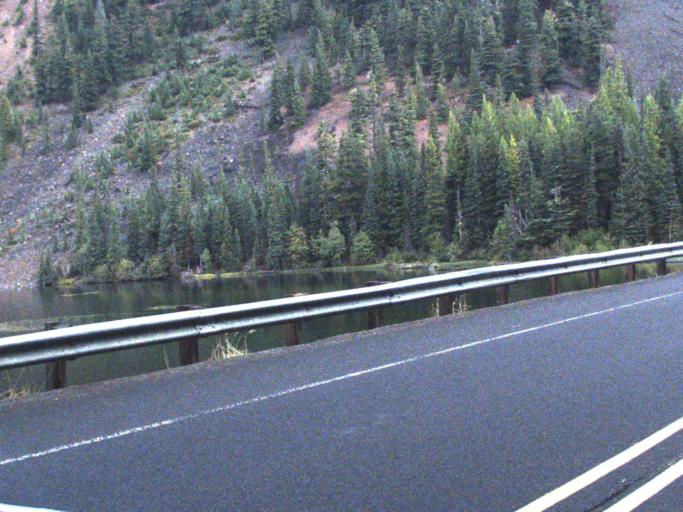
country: US
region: Washington
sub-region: Yakima County
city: Tieton
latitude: 46.6559
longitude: -121.3558
